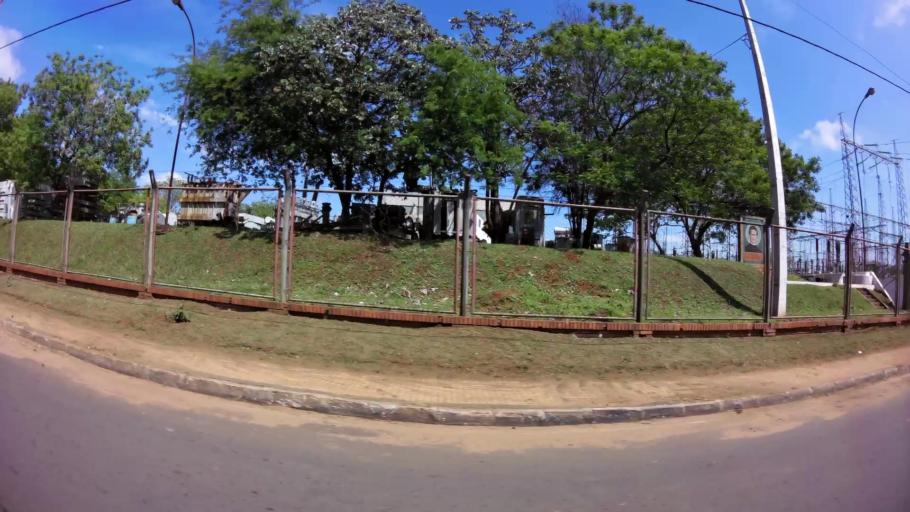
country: PY
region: Central
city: San Lorenzo
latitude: -25.3225
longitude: -57.5087
